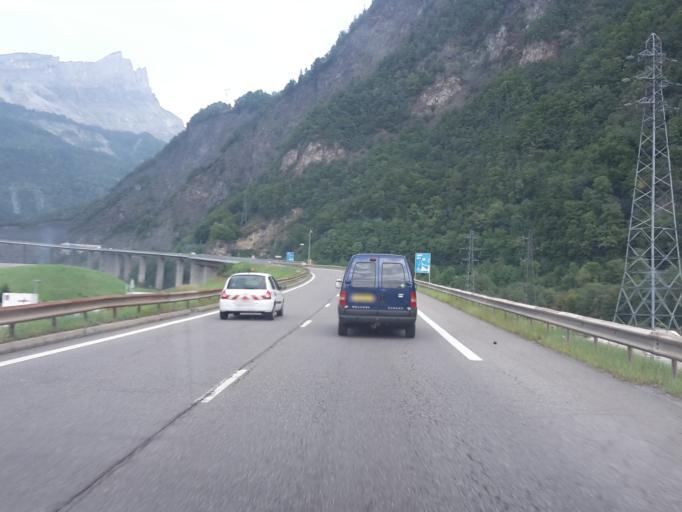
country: FR
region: Rhone-Alpes
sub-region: Departement de la Haute-Savoie
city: Saint-Gervais-les-Bains
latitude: 45.9184
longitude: 6.7257
